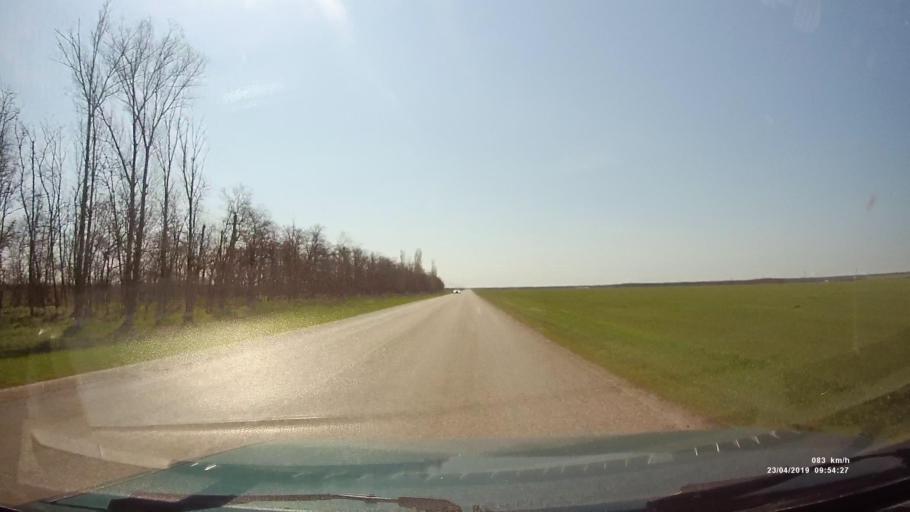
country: RU
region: Rostov
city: Orlovskiy
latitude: 46.8207
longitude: 42.0554
